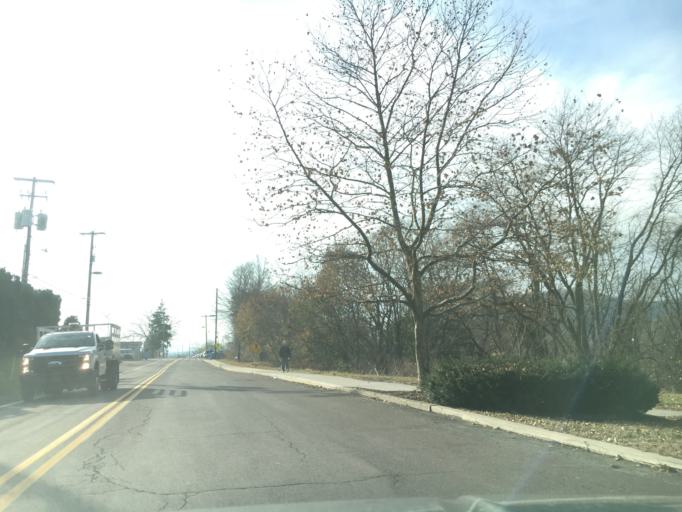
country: US
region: Pennsylvania
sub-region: Montour County
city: Danville
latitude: 40.9696
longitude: -76.6063
